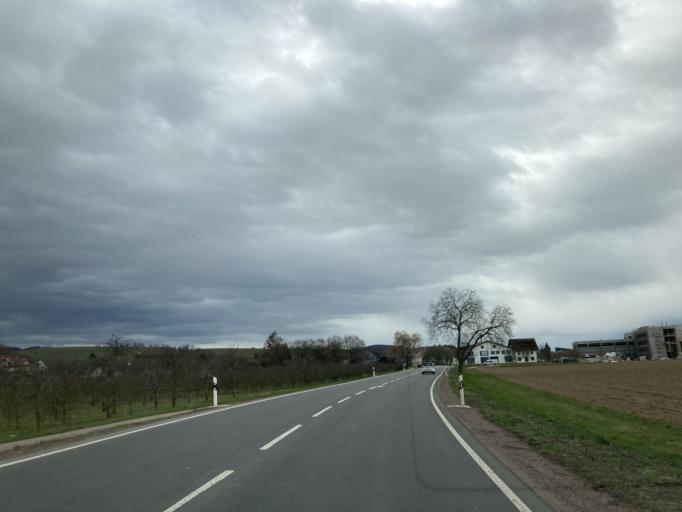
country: DE
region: Baden-Wuerttemberg
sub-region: Freiburg Region
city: Buggingen
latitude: 47.8349
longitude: 7.6230
